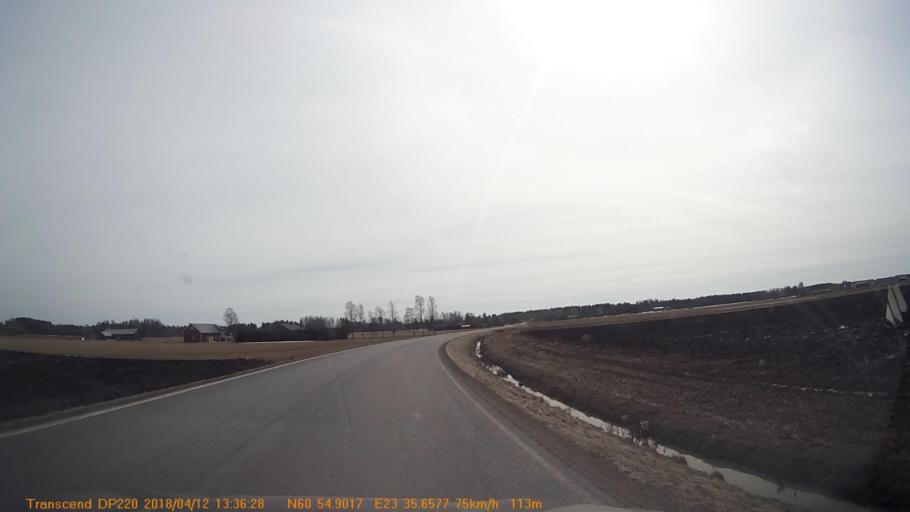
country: FI
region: Haeme
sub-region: Forssa
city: Forssa
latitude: 60.9147
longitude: 23.5944
